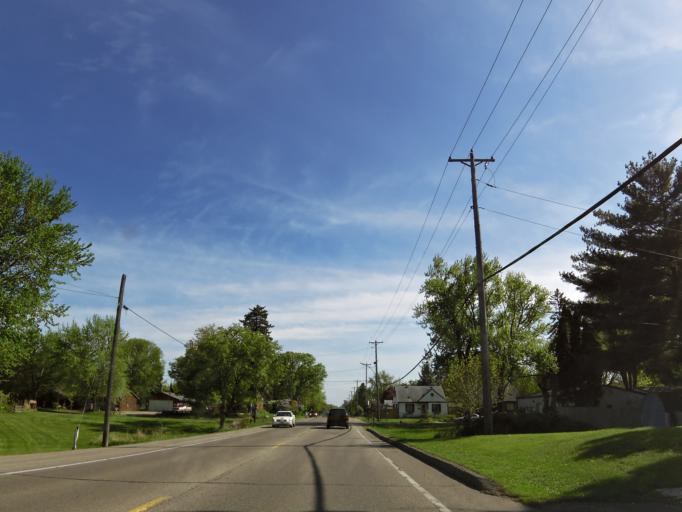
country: US
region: Minnesota
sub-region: Ramsey County
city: North Saint Paul
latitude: 45.0111
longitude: -92.9848
